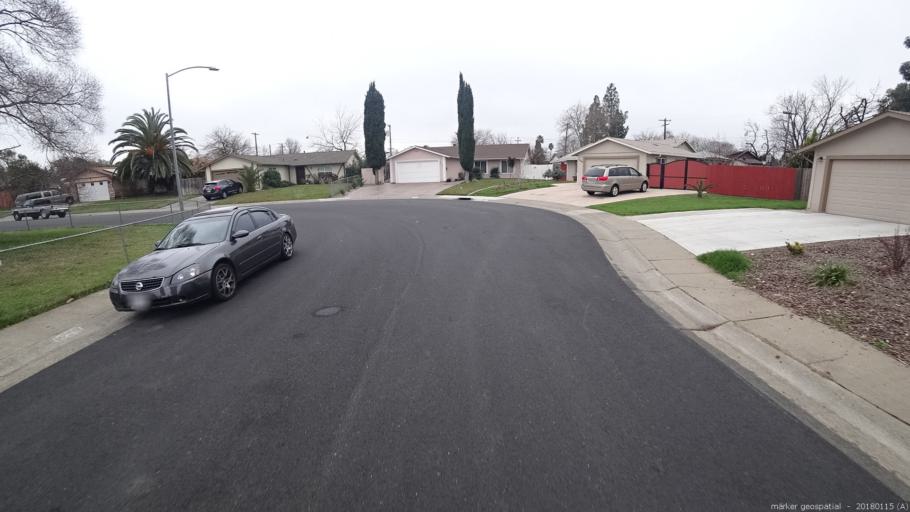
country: US
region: California
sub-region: Sacramento County
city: Rancho Cordova
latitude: 38.5868
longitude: -121.3024
